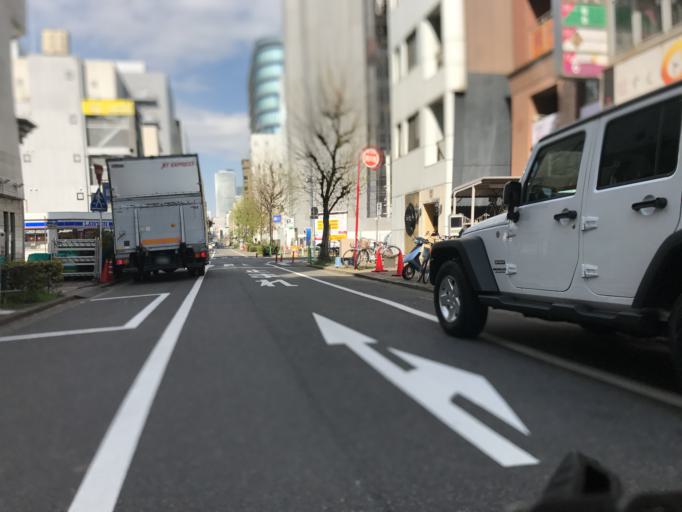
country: JP
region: Aichi
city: Nagoya-shi
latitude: 35.1725
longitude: 136.9035
